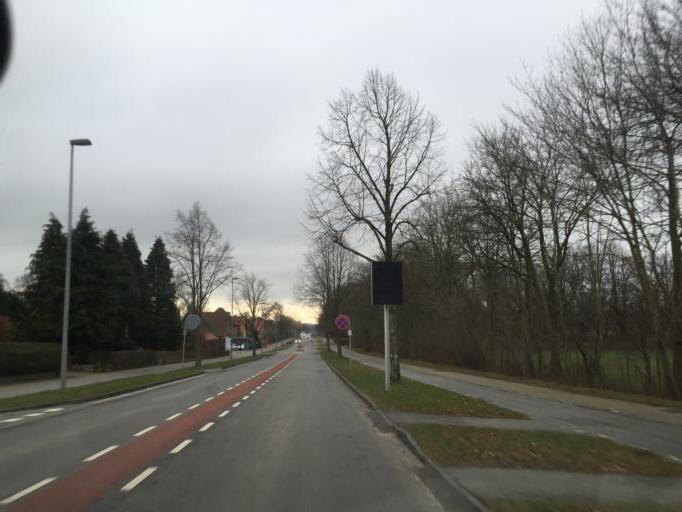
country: DK
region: South Denmark
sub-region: Haderslev Kommune
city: Haderslev
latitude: 55.2632
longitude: 9.4946
